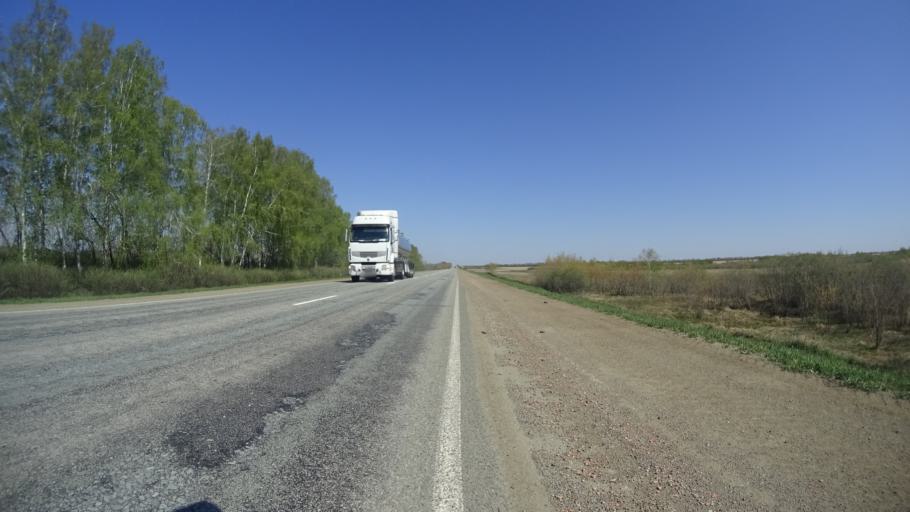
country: RU
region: Chelyabinsk
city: Troitsk
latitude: 54.1989
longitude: 61.4324
